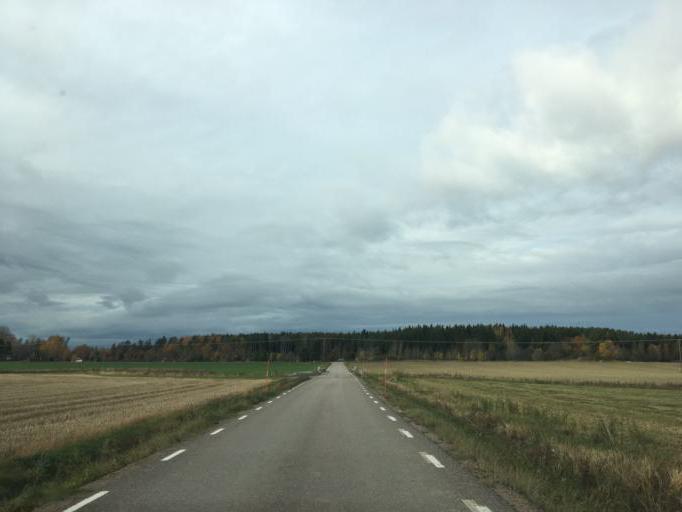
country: SE
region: Vaestmanland
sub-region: Hallstahammars Kommun
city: Kolback
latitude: 59.5503
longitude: 16.3408
